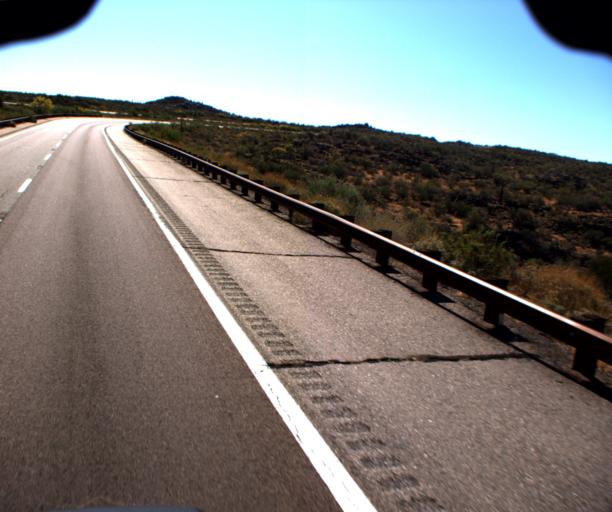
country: US
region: Arizona
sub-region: Yavapai County
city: Bagdad
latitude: 34.5012
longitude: -113.4026
